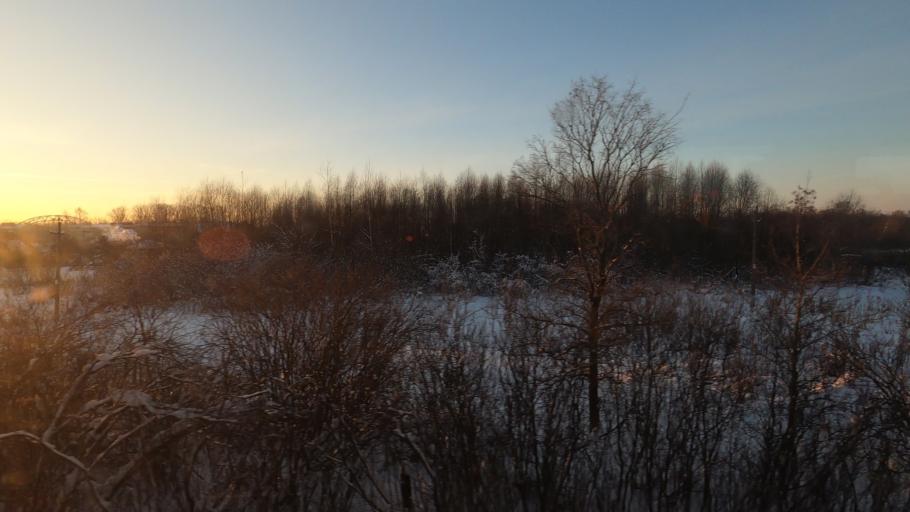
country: RU
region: Moskovskaya
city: Dmitrov
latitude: 56.3557
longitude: 37.5198
